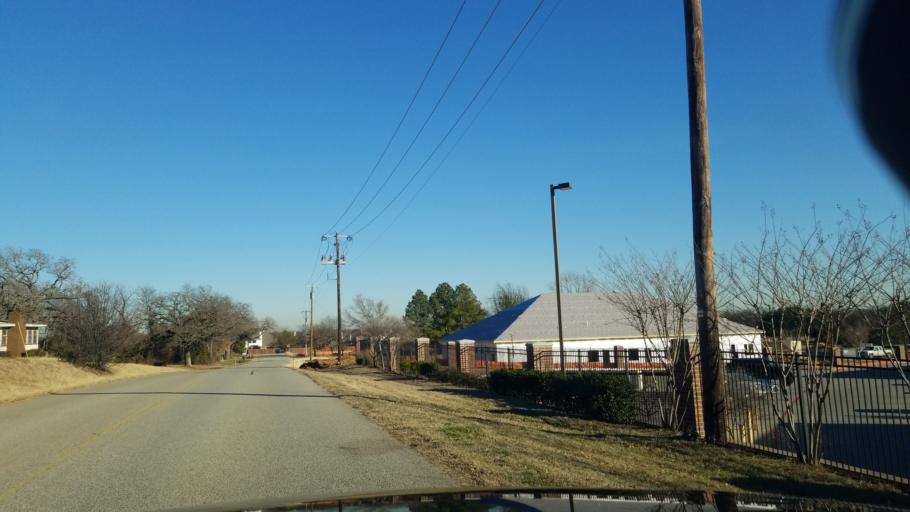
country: US
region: Texas
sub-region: Denton County
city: Corinth
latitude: 33.1545
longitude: -97.0553
